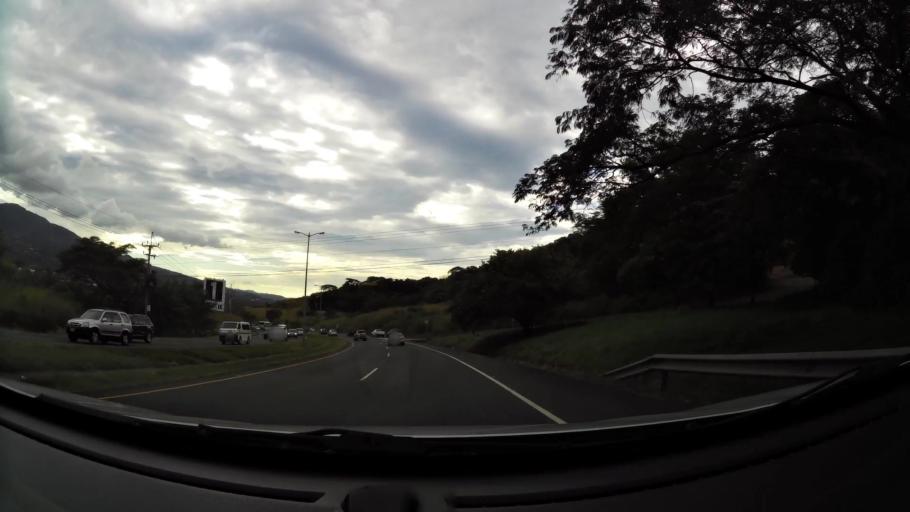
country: CR
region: San Jose
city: Santa Ana
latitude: 9.9486
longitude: -84.1763
